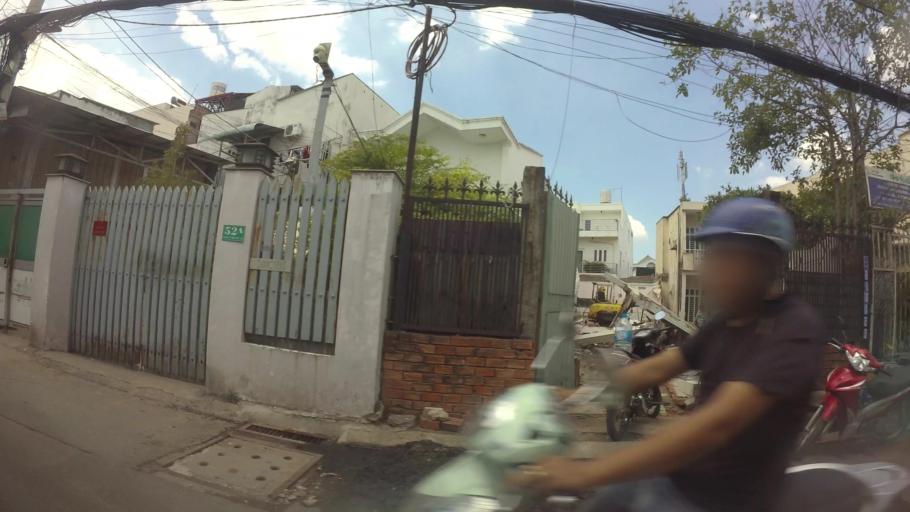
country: VN
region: Ho Chi Minh City
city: Quan Chin
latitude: 10.8220
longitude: 106.7605
